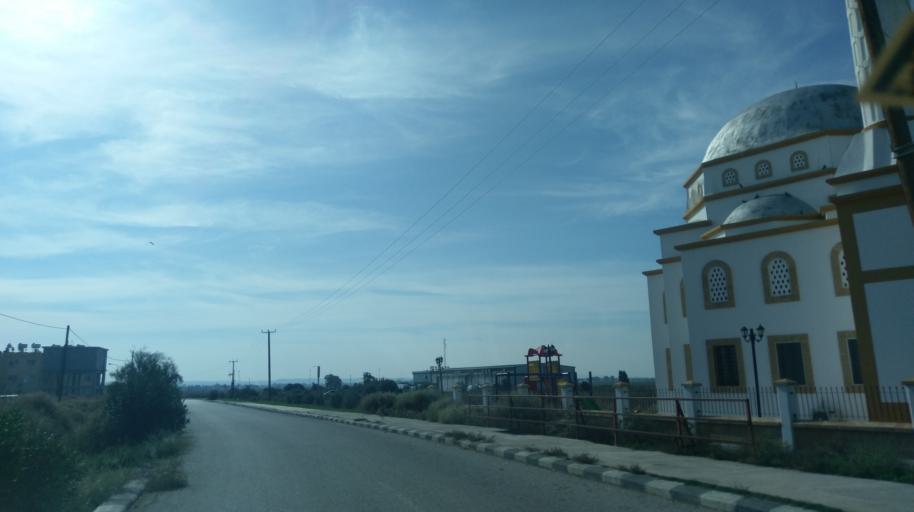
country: CY
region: Ammochostos
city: Lefkonoiko
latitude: 35.1905
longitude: 33.6397
